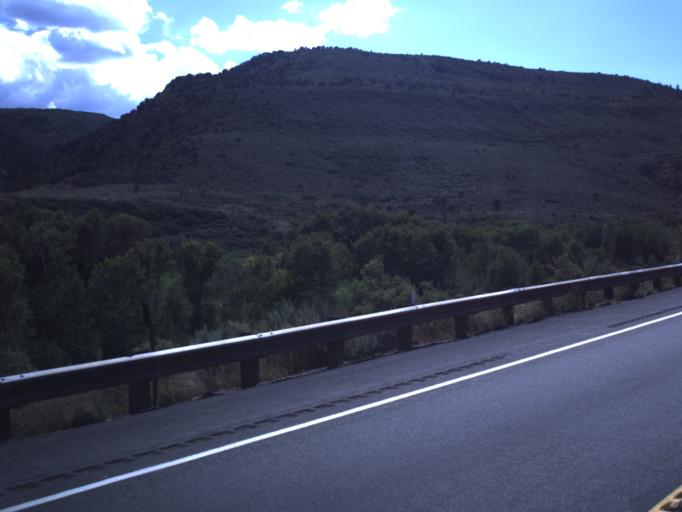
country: US
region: Utah
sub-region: Duchesne County
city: Duchesne
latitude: 40.1987
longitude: -110.8976
